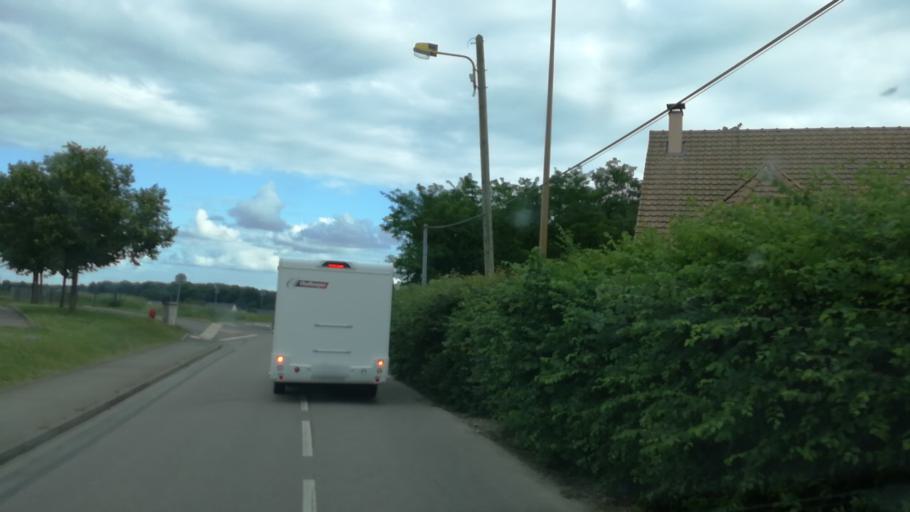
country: FR
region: Haute-Normandie
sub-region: Departement de l'Eure
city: Bourg-Achard
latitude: 49.3469
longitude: 0.8178
